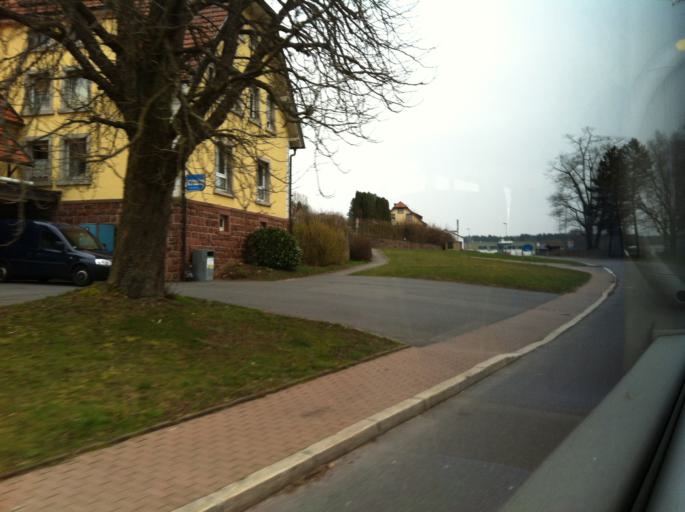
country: DE
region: Baden-Wuerttemberg
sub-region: Karlsruhe Region
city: Limbach
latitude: 49.4526
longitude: 9.1816
